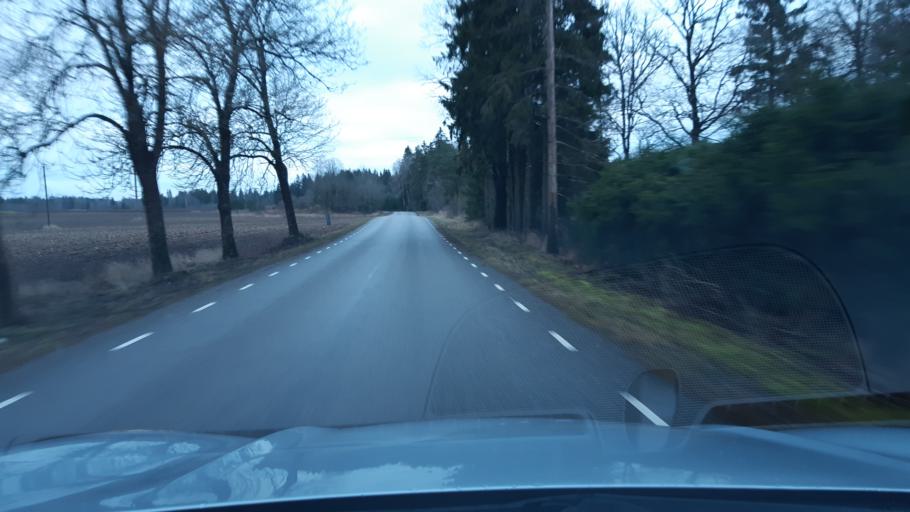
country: EE
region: Harju
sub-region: Saue linn
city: Saue
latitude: 59.2237
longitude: 24.5247
